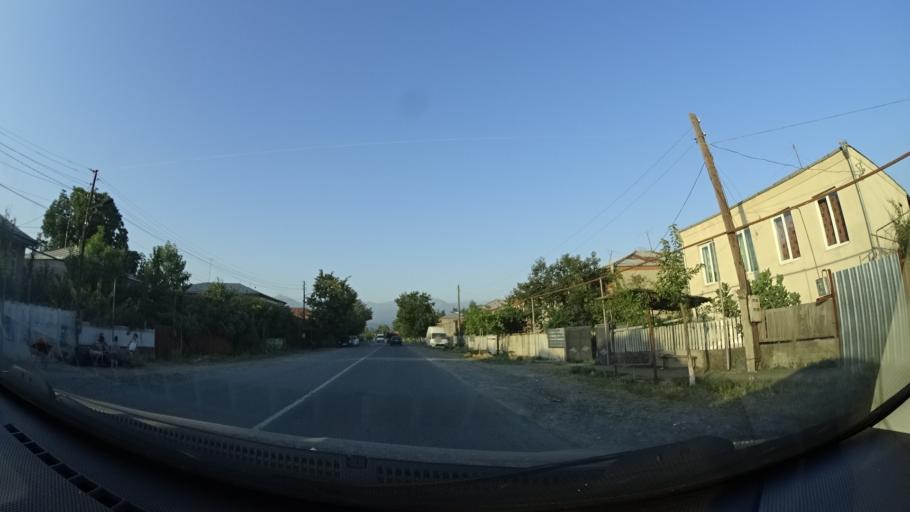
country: GE
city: Bagdadi
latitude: 41.8096
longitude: 46.0099
